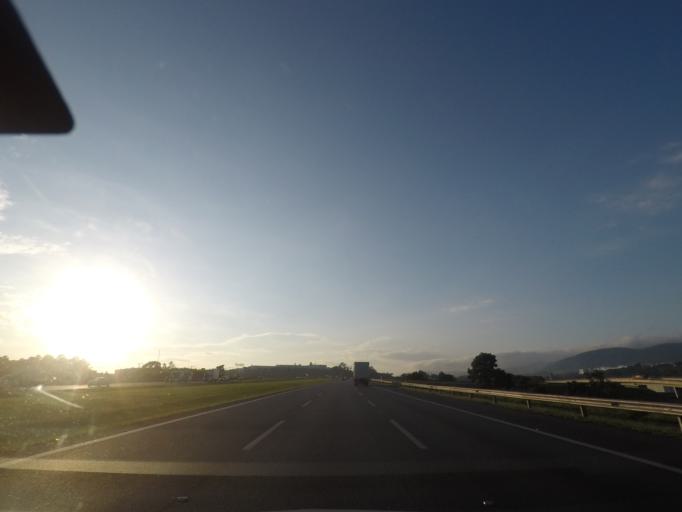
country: BR
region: Sao Paulo
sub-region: Jundiai
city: Jundiai
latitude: -23.1699
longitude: -46.9406
